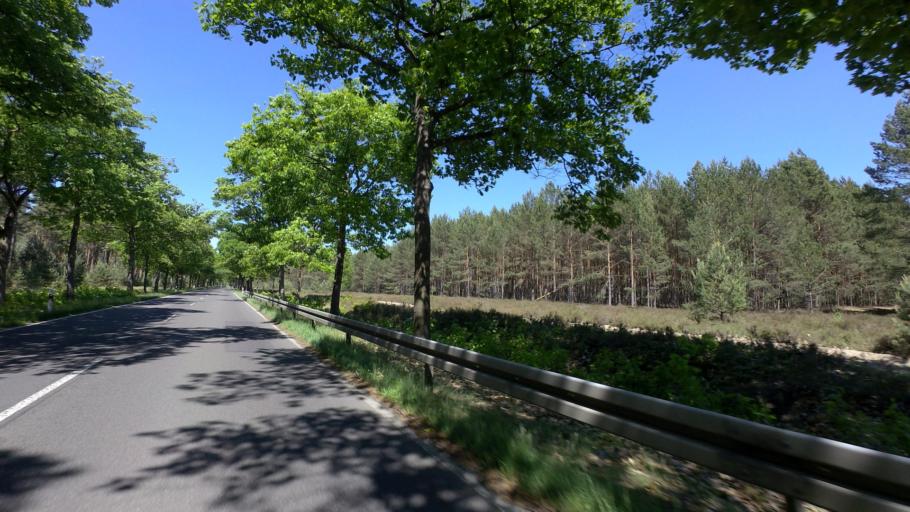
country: DE
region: Brandenburg
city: Drehnow
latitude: 51.9035
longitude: 14.3554
